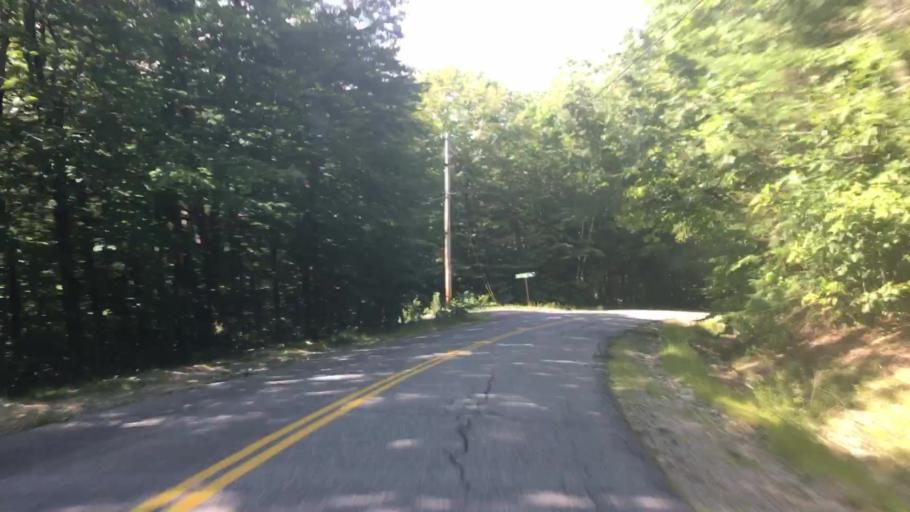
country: US
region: Maine
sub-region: Androscoggin County
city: Poland
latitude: 44.0122
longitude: -70.3843
